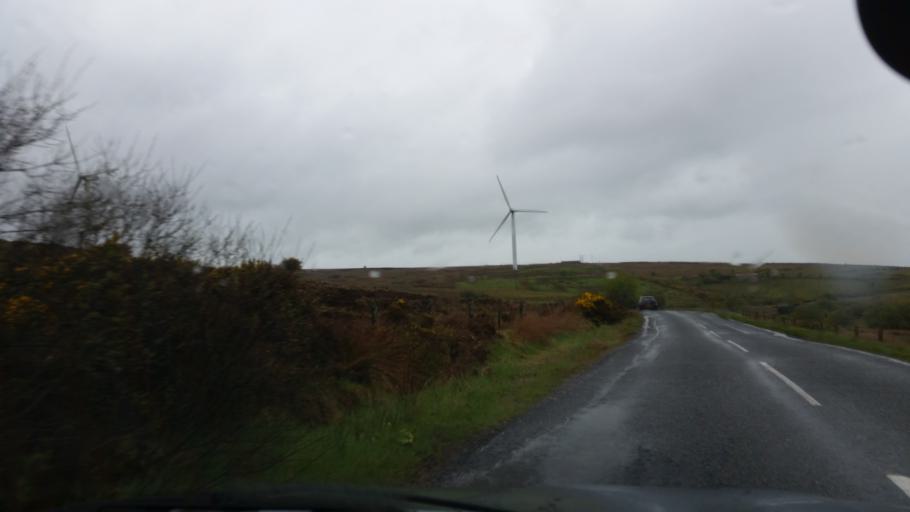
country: GB
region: Northern Ireland
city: Fintona
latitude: 54.4516
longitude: -7.3230
